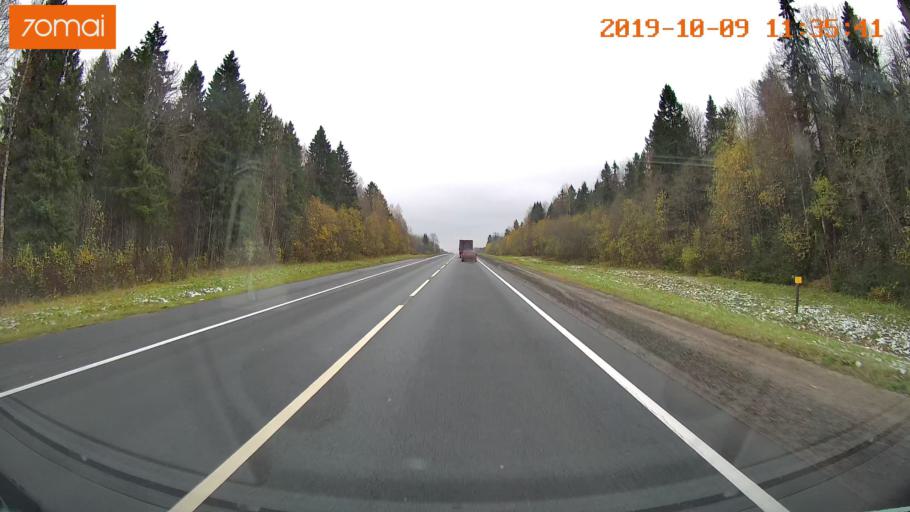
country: RU
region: Vologda
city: Gryazovets
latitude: 59.0002
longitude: 40.1287
